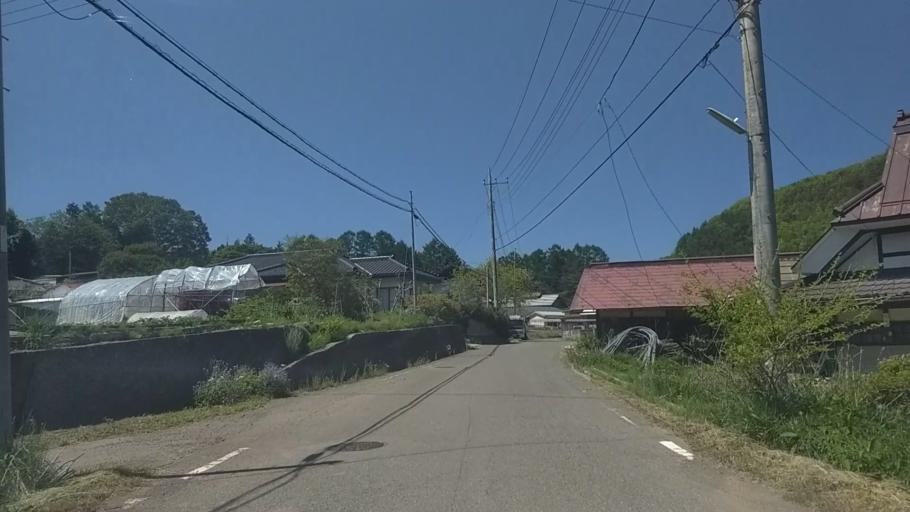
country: JP
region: Yamanashi
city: Nirasaki
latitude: 35.8733
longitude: 138.4529
